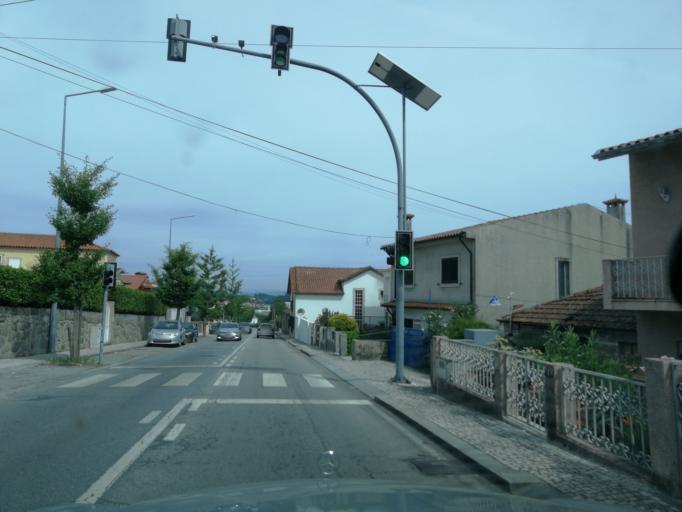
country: PT
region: Braga
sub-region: Vila Nova de Famalicao
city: Calendario
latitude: 41.4145
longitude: -8.5308
